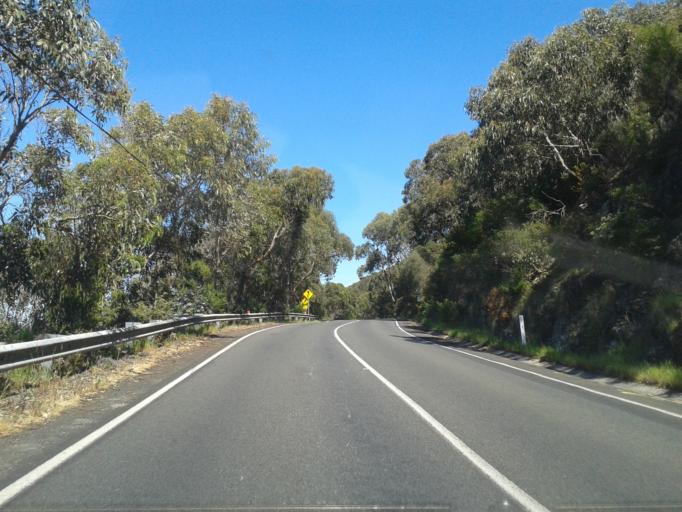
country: AU
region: Victoria
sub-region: Surf Coast
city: Anglesea
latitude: -38.4865
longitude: 144.0284
